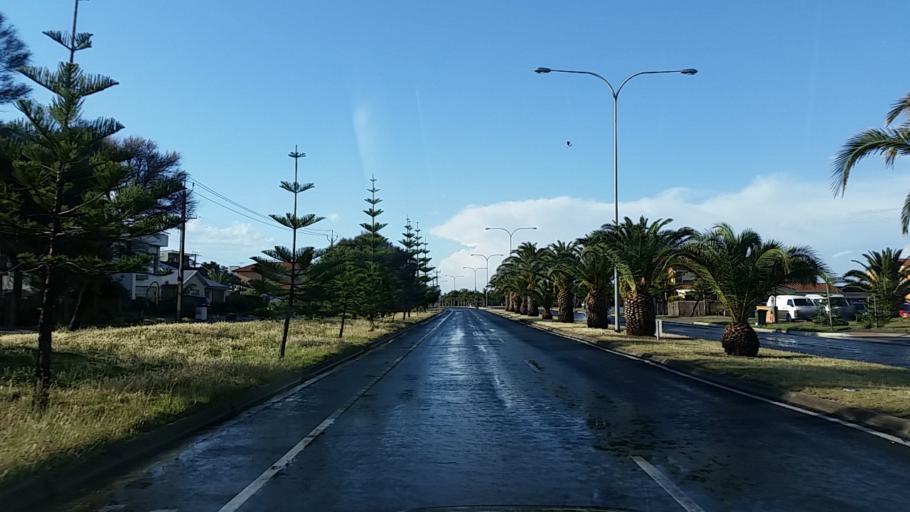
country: AU
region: South Australia
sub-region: Charles Sturt
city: Grange
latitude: -34.8884
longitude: 138.4870
